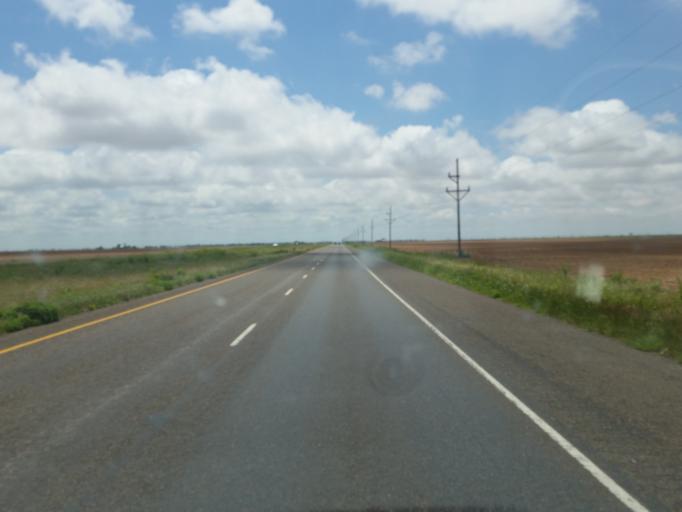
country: US
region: Texas
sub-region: Lubbock County
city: Slaton
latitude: 33.3880
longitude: -101.5960
